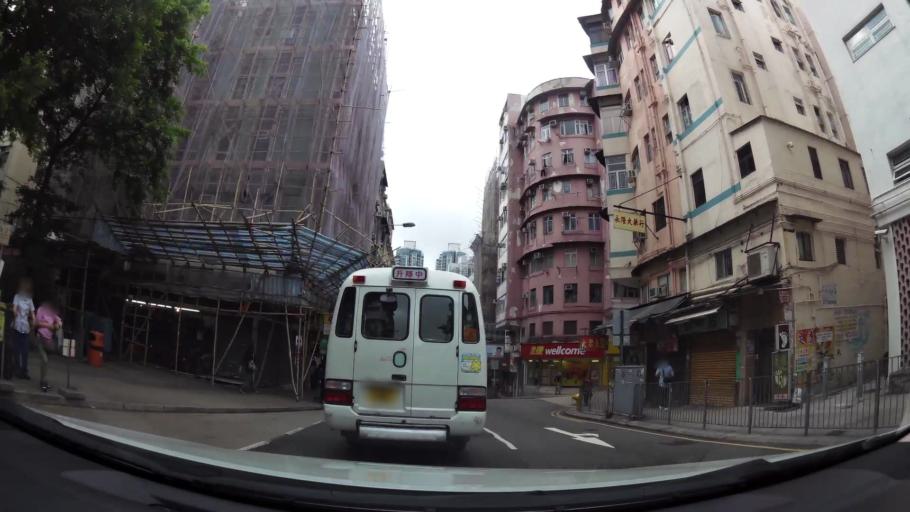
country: HK
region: Wong Tai Sin
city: Wong Tai Sin
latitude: 22.3449
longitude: 114.1975
